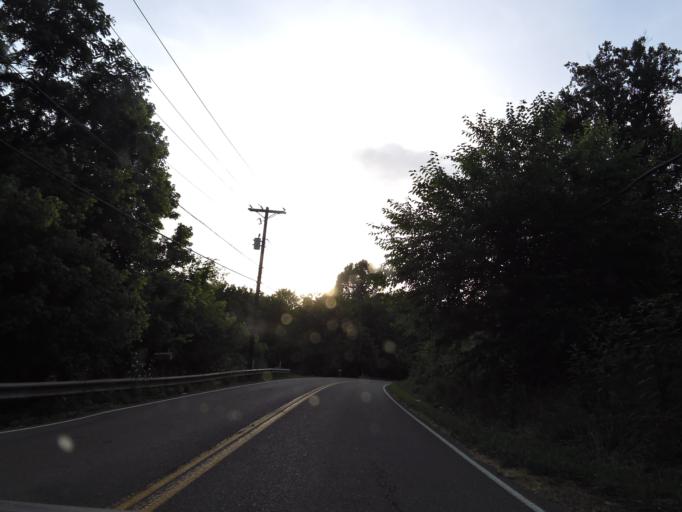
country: US
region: Tennessee
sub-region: Knox County
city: Knoxville
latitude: 35.9802
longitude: -83.8532
